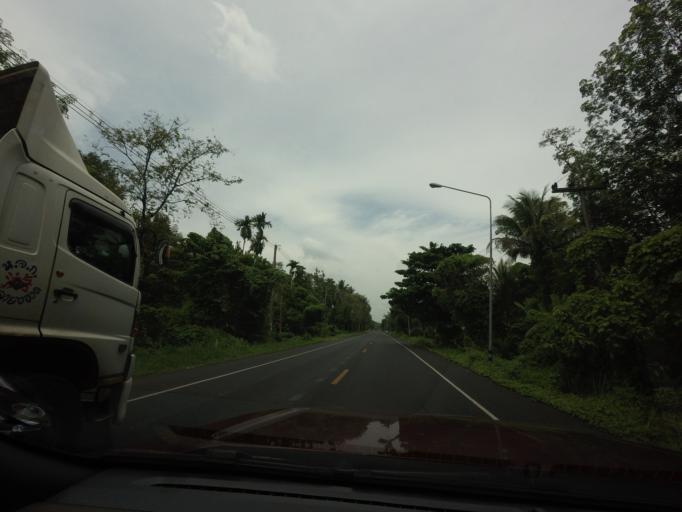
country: TH
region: Pattani
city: Mae Lan
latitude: 6.6511
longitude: 101.3027
